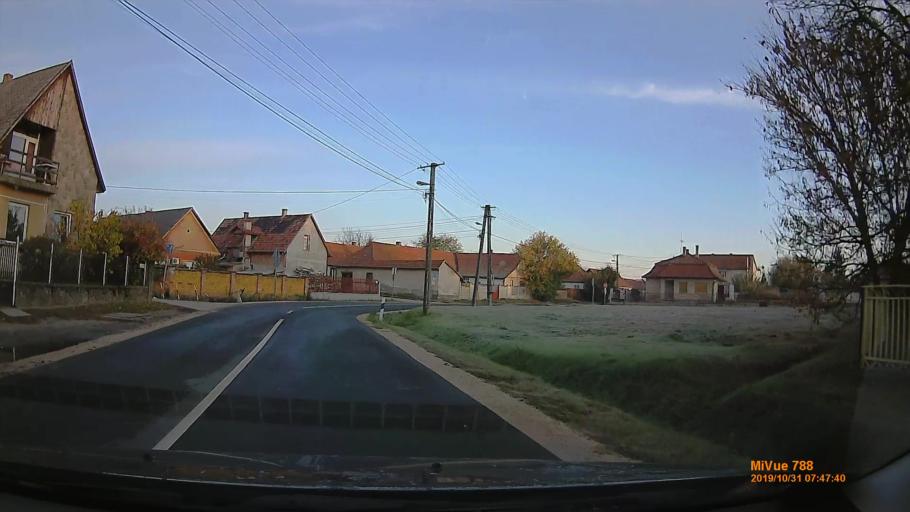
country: HU
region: Pest
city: Pilis
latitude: 47.2884
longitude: 19.5501
